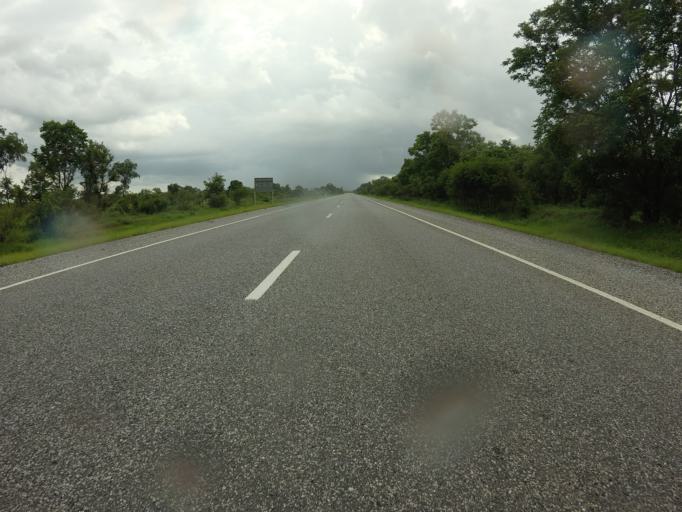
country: GH
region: Northern
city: Tamale
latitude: 9.1439
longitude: -1.3580
